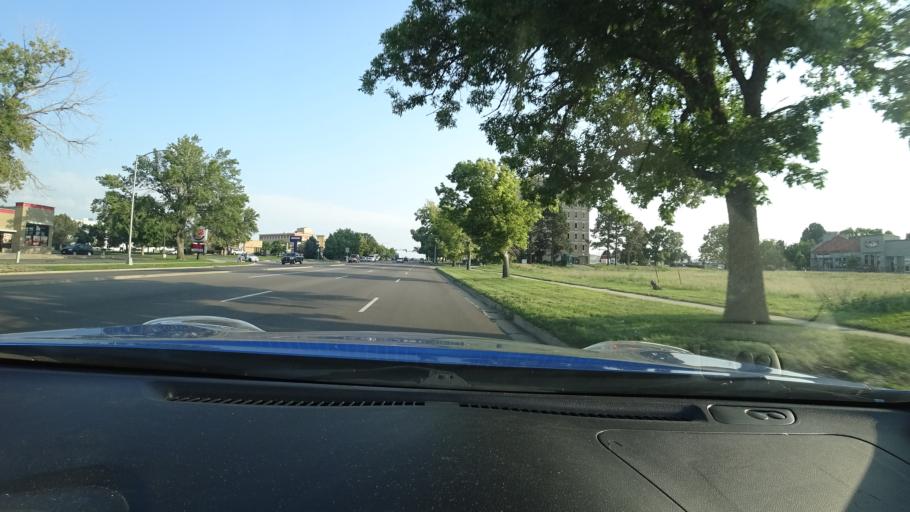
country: US
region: Colorado
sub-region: Adams County
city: Aurora
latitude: 39.7804
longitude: -104.8471
